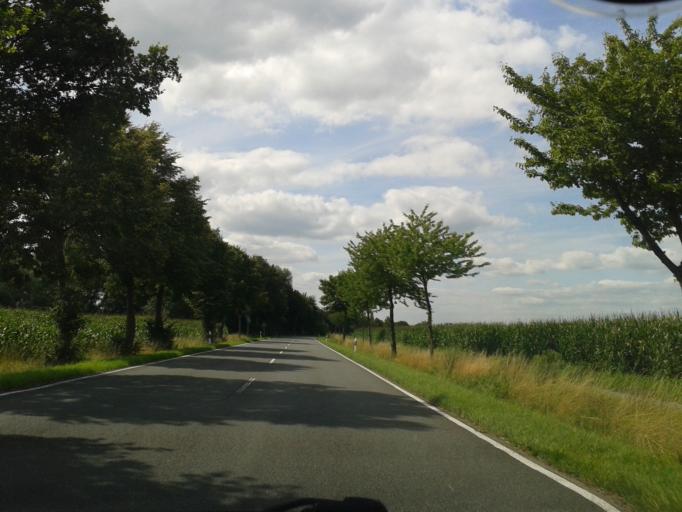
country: DE
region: North Rhine-Westphalia
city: Bad Lippspringe
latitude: 51.7609
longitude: 8.8115
